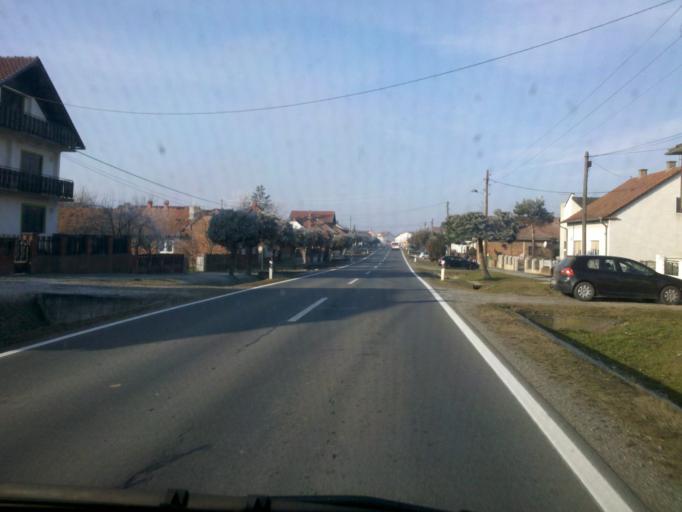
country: HR
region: Koprivnicko-Krizevacka
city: Kalinovac
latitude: 45.9807
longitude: 17.1623
